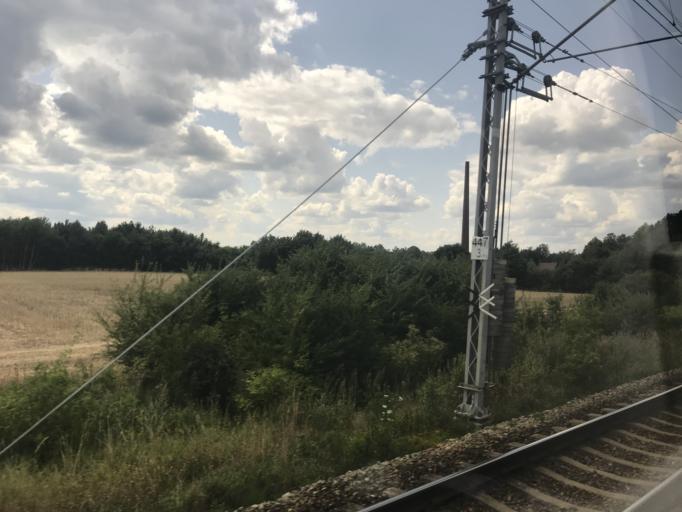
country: PL
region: Lubusz
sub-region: Powiat sulecinski
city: Torzym
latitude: 52.3231
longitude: 15.0041
